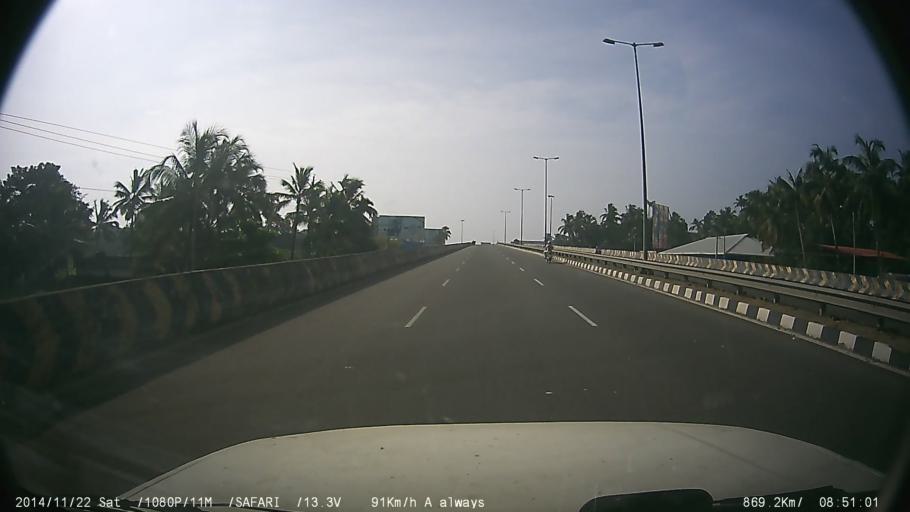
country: IN
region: Kerala
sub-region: Thrissur District
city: Trichur
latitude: 10.4532
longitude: 76.2581
